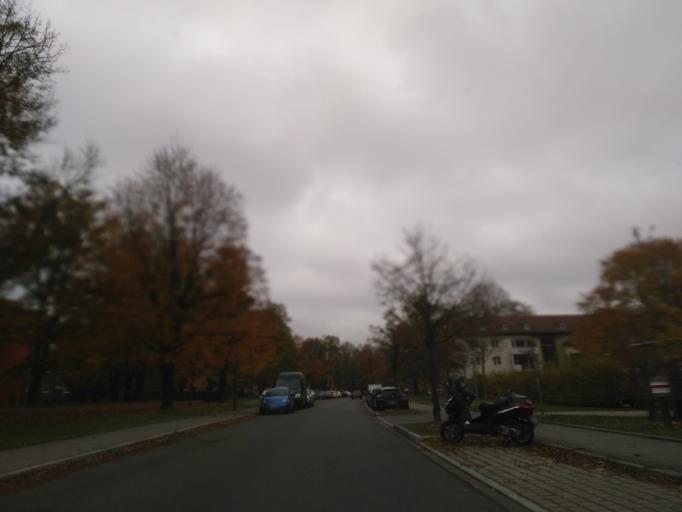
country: DE
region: Bavaria
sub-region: Upper Bavaria
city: Unterhaching
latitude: 48.0923
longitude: 11.5923
